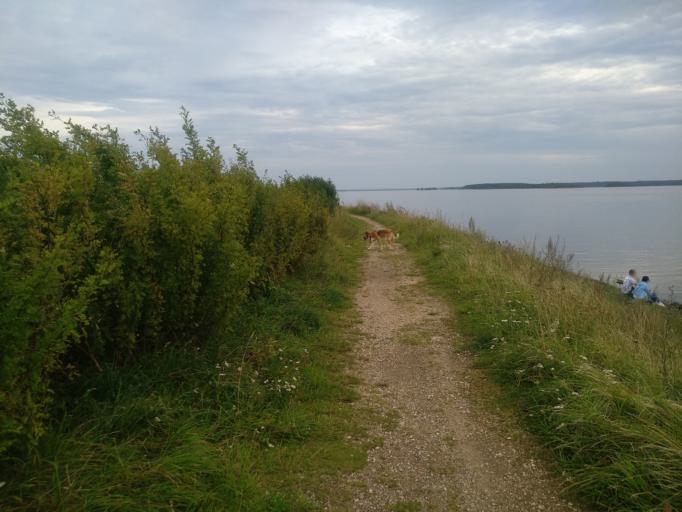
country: RU
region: Tverskaya
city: Vyshniy Volochek
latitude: 57.6064
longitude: 34.4968
